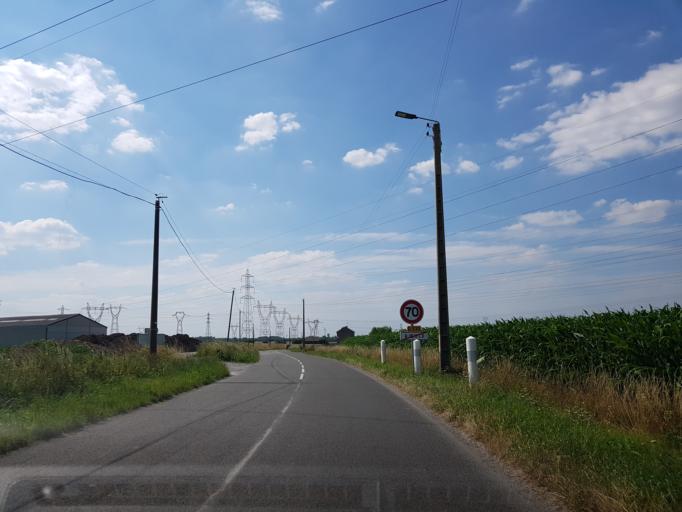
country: FR
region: Nord-Pas-de-Calais
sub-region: Departement du Nord
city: Roeulx
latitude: 50.3146
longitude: 3.3310
